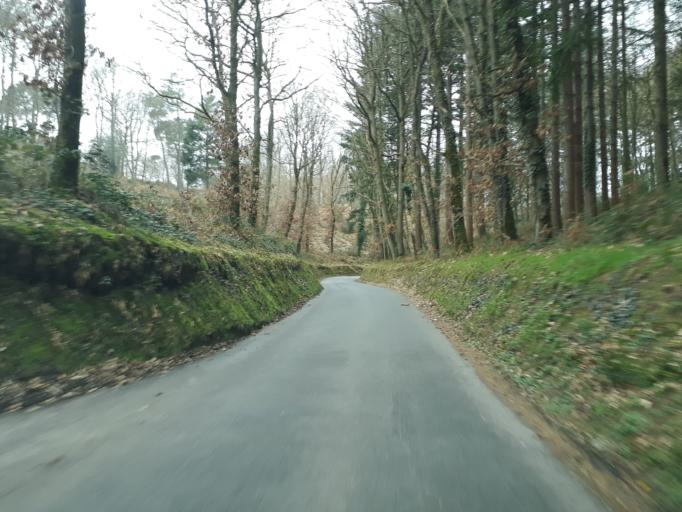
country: FR
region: Haute-Normandie
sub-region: Departement de la Seine-Maritime
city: Les Loges
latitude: 49.6806
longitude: 0.2558
